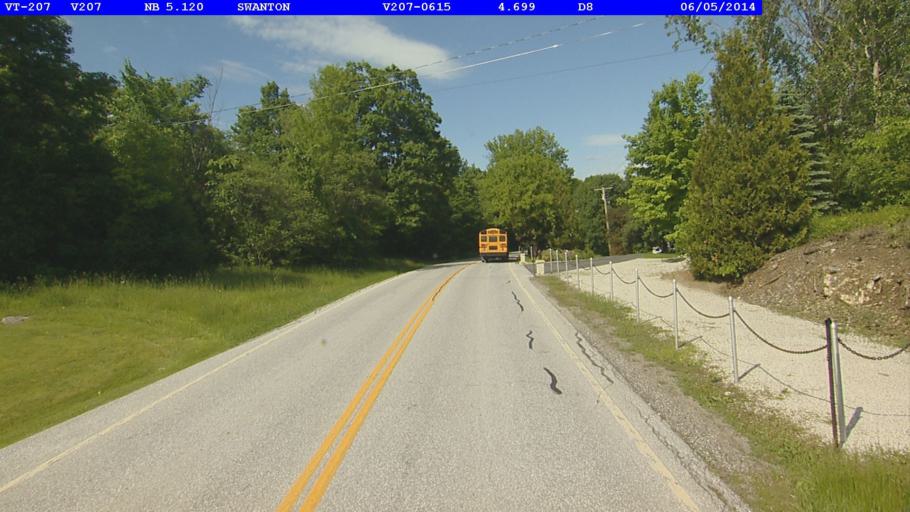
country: US
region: Vermont
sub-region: Franklin County
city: Swanton
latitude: 44.9109
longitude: -73.0600
